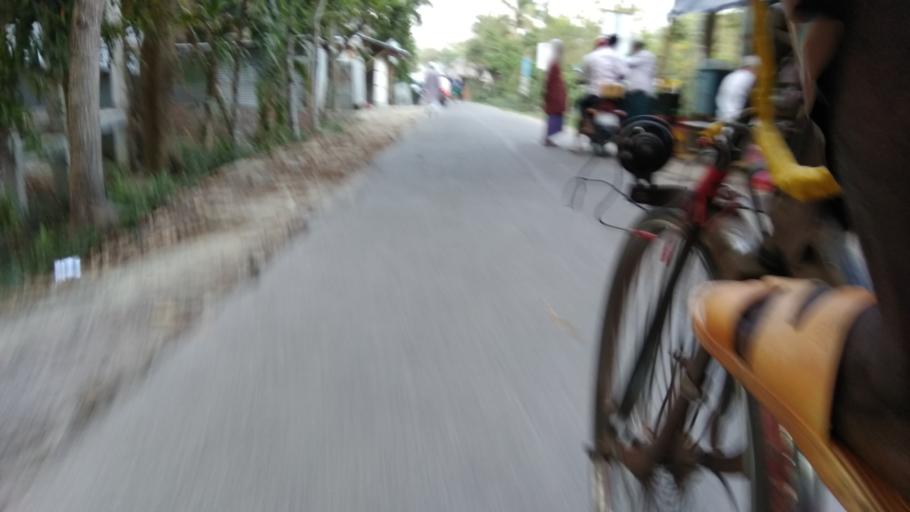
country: BD
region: Barisal
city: Mehendiganj
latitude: 22.9393
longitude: 90.4091
